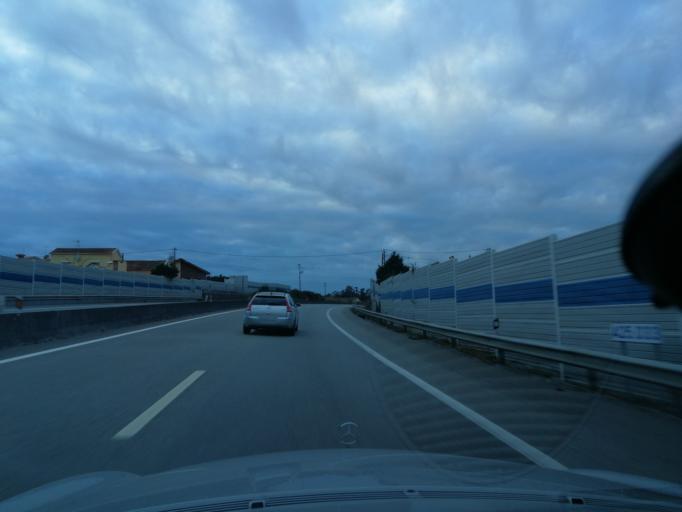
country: PT
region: Aveiro
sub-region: Albergaria-A-Velha
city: Albergaria-a-Velha
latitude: 40.6872
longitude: -8.5115
